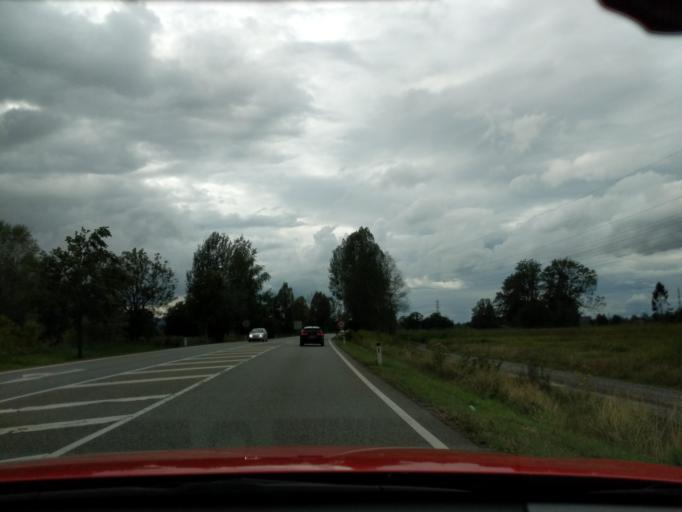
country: AT
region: Vorarlberg
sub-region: Politischer Bezirk Bregenz
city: Schwarzach
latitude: 47.4387
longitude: 9.7501
